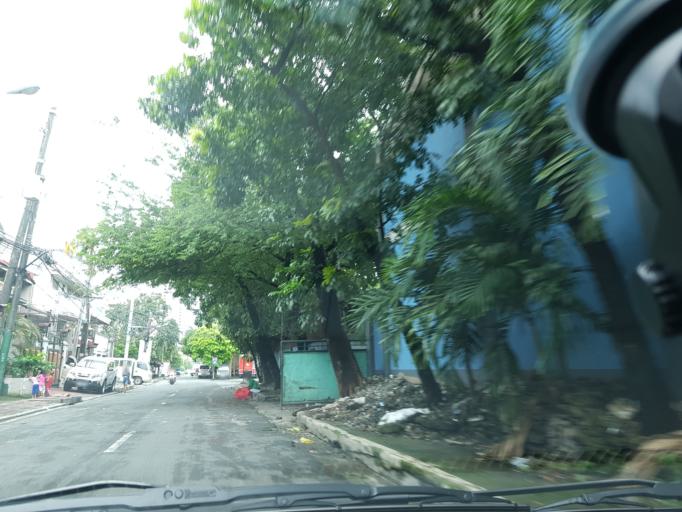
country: PH
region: Metro Manila
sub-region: Pasig
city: Pasig City
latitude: 14.5672
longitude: 121.0695
